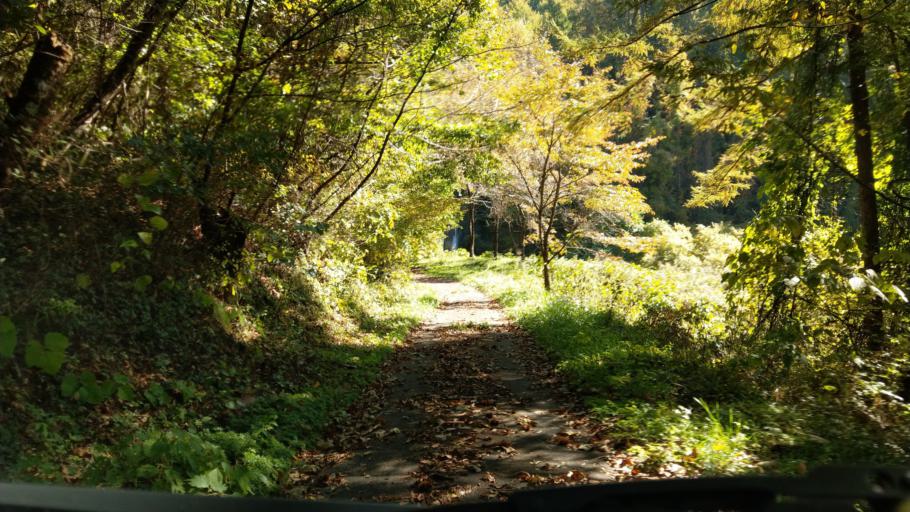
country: JP
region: Nagano
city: Komoro
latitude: 36.3746
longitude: 138.4240
